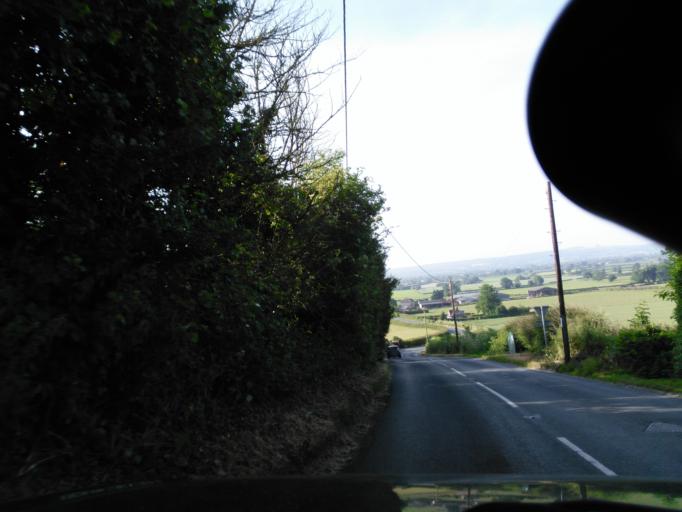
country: GB
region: England
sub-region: Wiltshire
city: Seend
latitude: 51.3467
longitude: -2.0874
